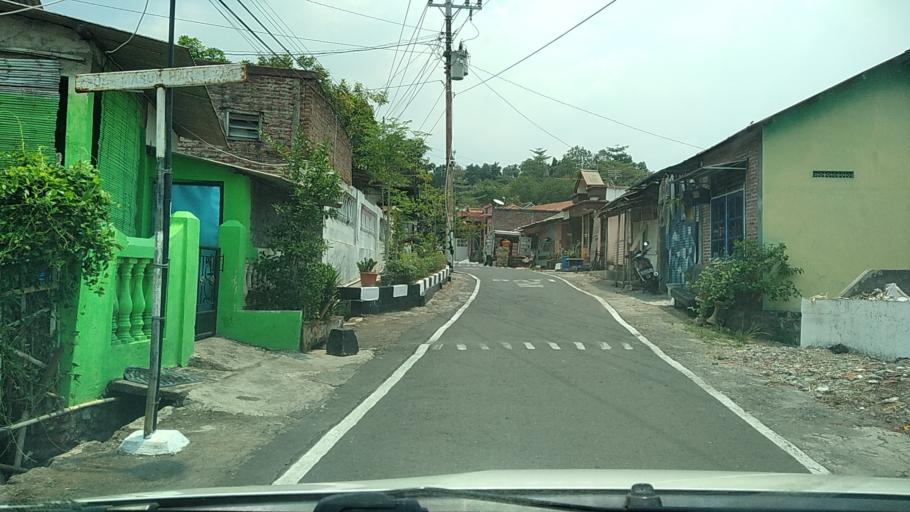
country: ID
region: Central Java
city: Semarang
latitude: -6.9885
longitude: 110.3630
